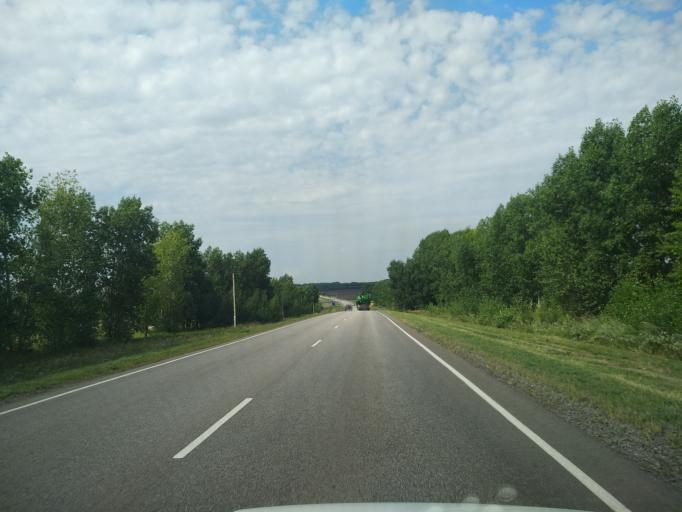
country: RU
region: Lipetsk
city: Dobrinka
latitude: 51.8890
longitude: 40.4356
